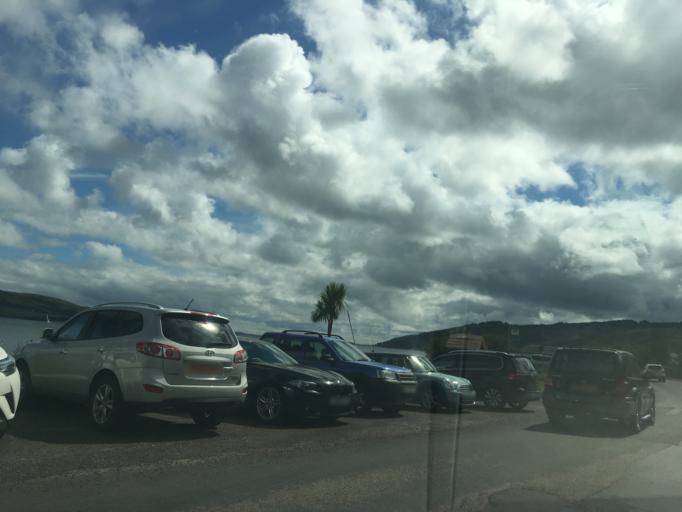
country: GB
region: Scotland
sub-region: Argyll and Bute
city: Tarbert
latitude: 55.9017
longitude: -5.2404
